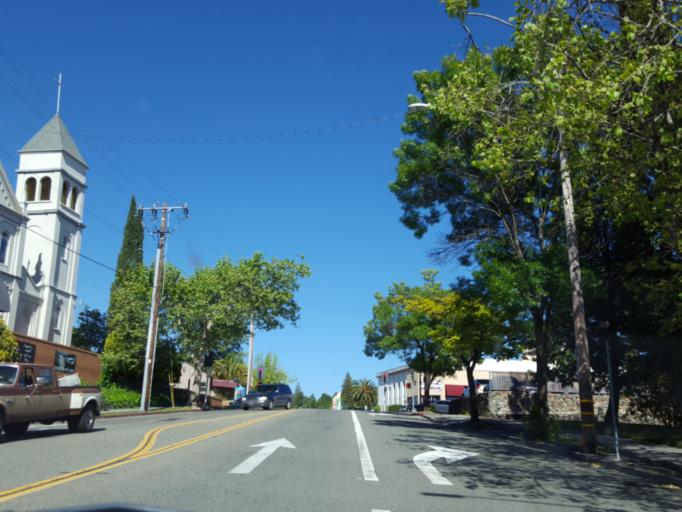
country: US
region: California
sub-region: Placer County
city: Auburn
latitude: 38.8980
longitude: -121.0740
